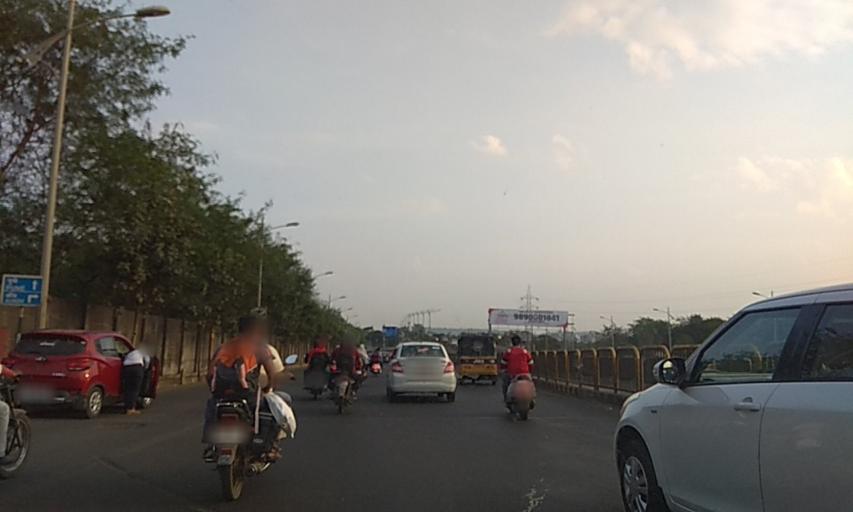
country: IN
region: Maharashtra
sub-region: Pune Division
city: Khadki
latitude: 18.5725
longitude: 73.8076
